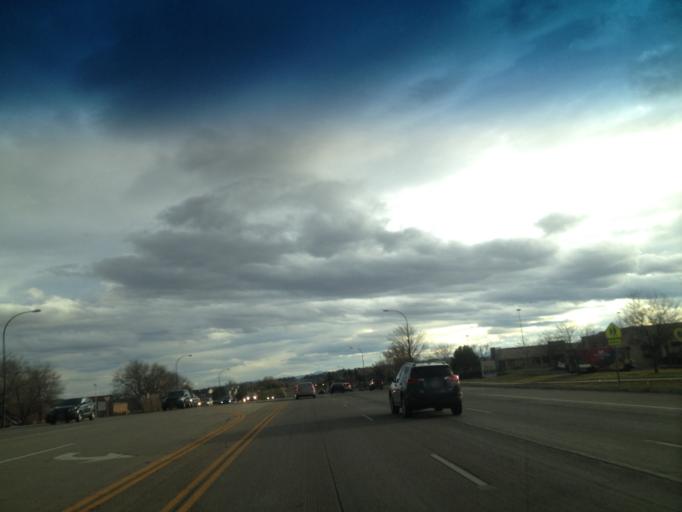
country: US
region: Colorado
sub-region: Adams County
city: Westminster
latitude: 39.8591
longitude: -105.0817
